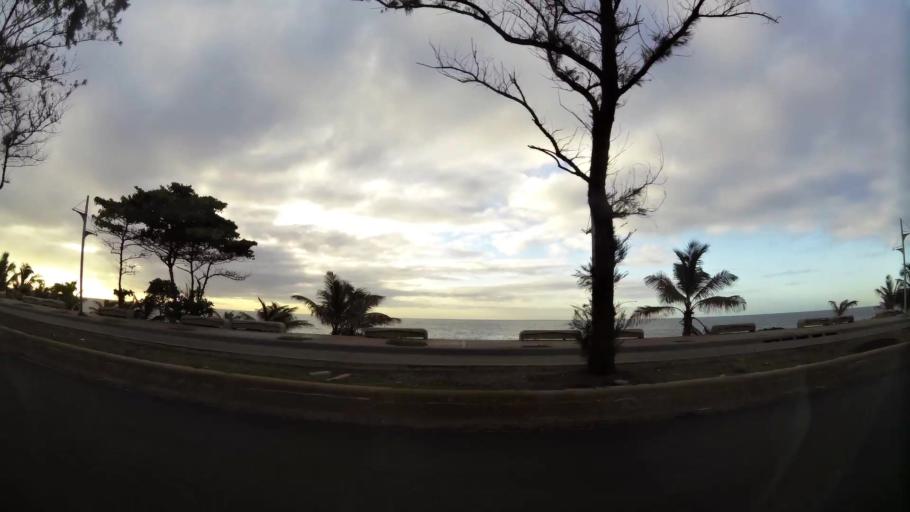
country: DO
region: Nacional
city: Bella Vista
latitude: 18.4407
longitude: -69.9315
